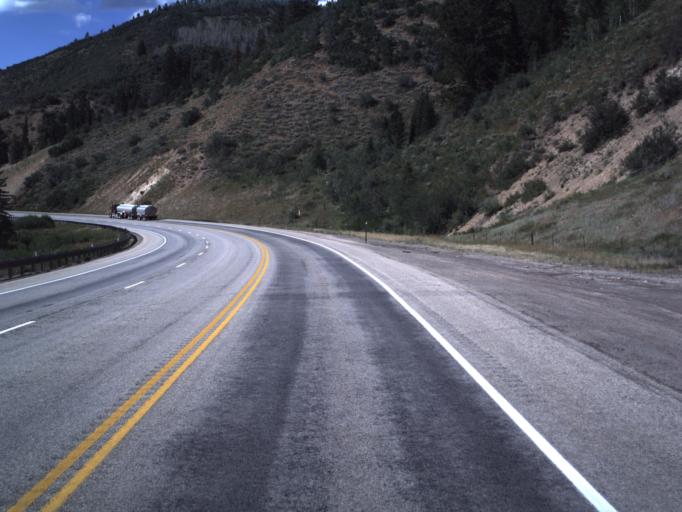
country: US
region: Utah
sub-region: Wasatch County
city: Heber
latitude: 40.3358
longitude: -111.2611
